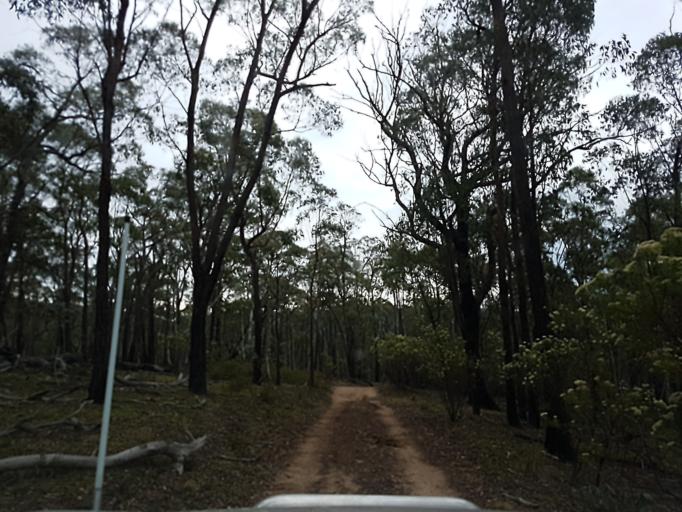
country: AU
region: New South Wales
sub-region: Snowy River
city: Jindabyne
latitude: -36.8707
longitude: 148.3293
